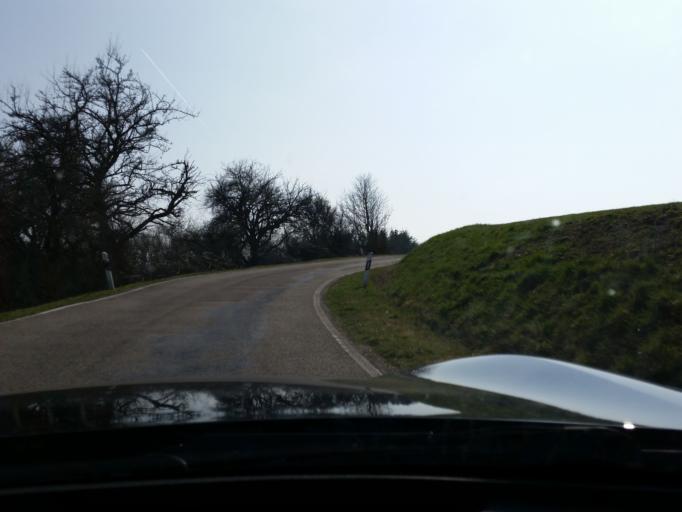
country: DE
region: Baden-Wuerttemberg
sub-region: Regierungsbezirk Stuttgart
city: Jagsthausen
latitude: 49.3597
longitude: 9.4647
